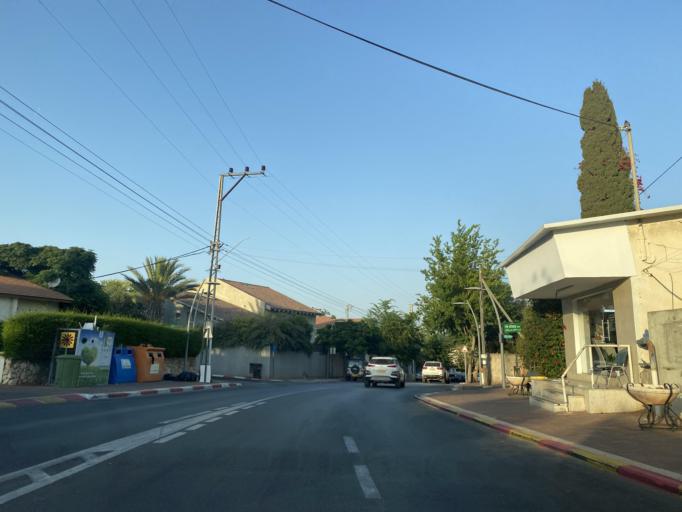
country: IL
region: Tel Aviv
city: Ramat HaSharon
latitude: 32.1356
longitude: 34.8527
